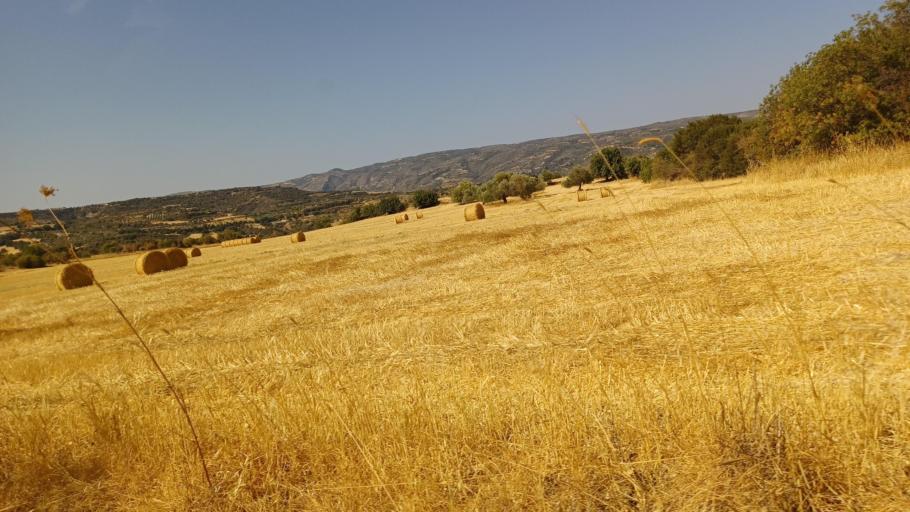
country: CY
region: Pafos
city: Polis
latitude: 34.9663
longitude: 32.4931
